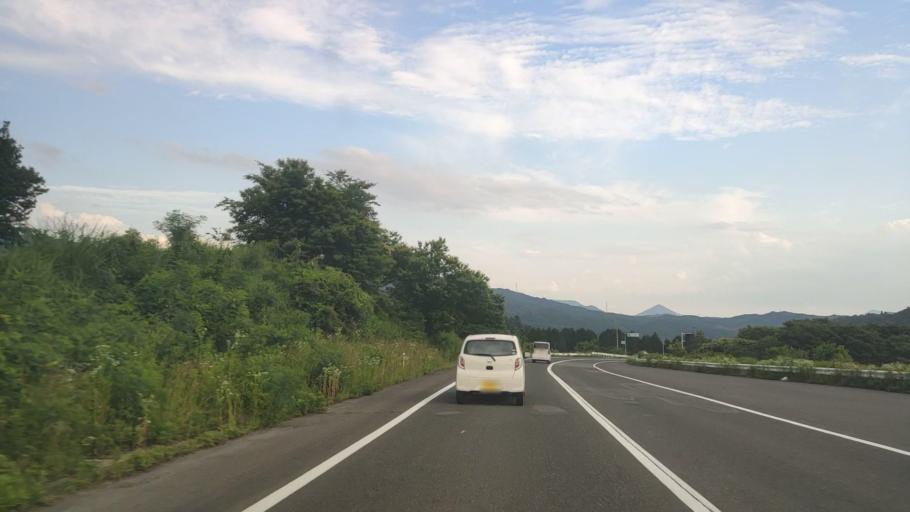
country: JP
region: Tottori
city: Kurayoshi
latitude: 35.2941
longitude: 133.7364
